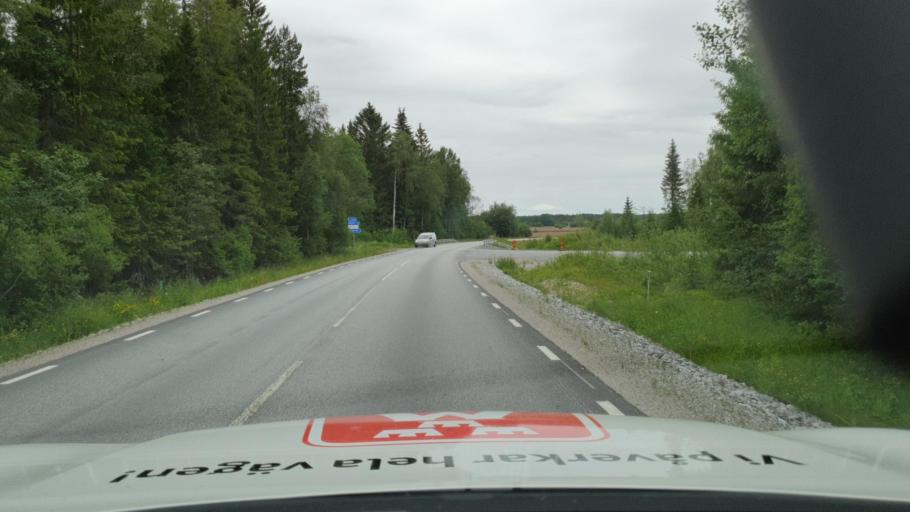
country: SE
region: Vaesterbotten
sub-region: Nordmalings Kommun
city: Nordmaling
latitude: 63.5703
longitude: 19.4256
